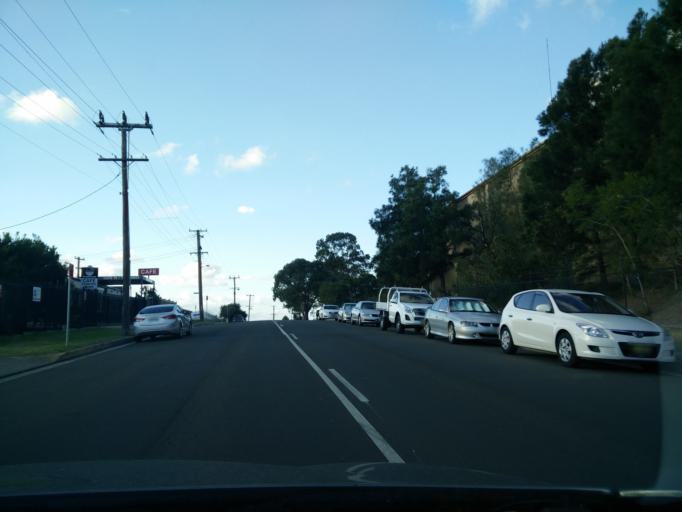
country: AU
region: New South Wales
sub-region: Wollongong
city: Cordeaux Heights
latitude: -34.4598
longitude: 150.8452
